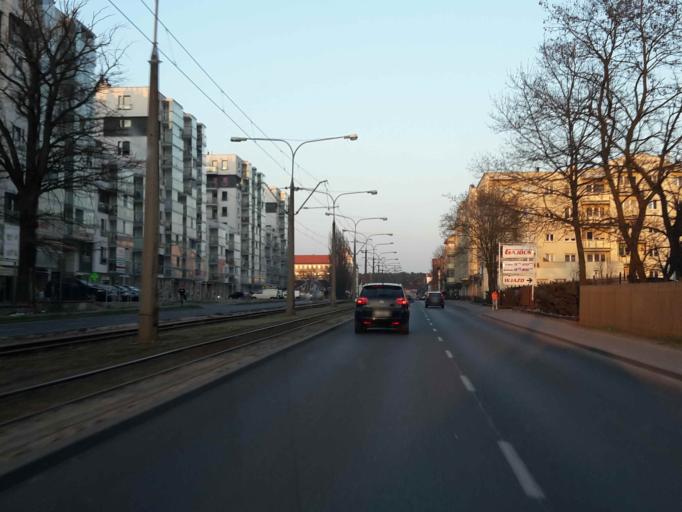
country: PL
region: Kujawsko-Pomorskie
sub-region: Torun
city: Torun
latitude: 53.0139
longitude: 18.5752
